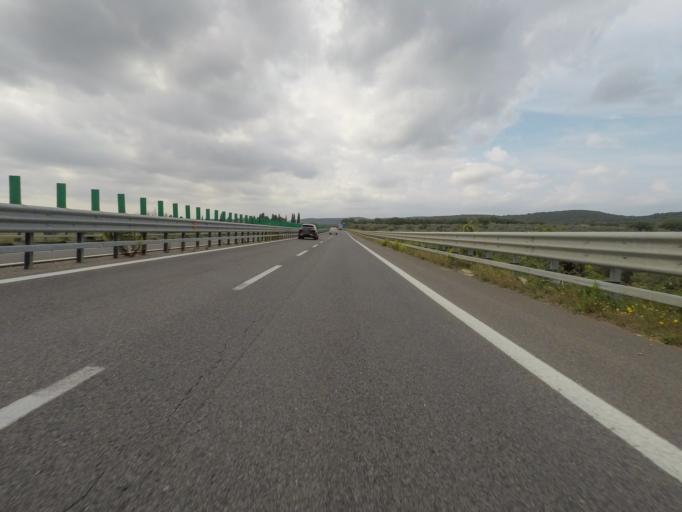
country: IT
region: Tuscany
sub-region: Provincia di Grosseto
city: Bagno Roselle
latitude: 42.8537
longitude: 11.1702
